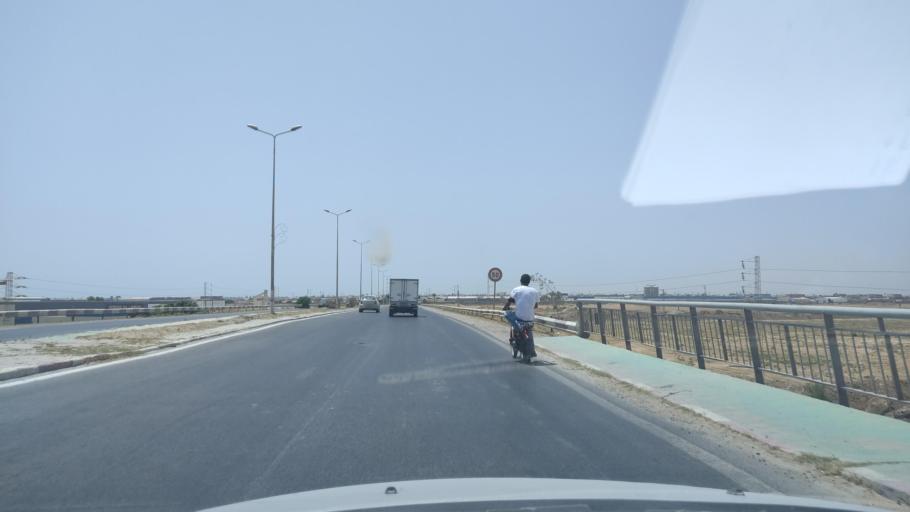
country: TN
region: Safaqis
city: Sfax
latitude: 34.7055
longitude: 10.7212
